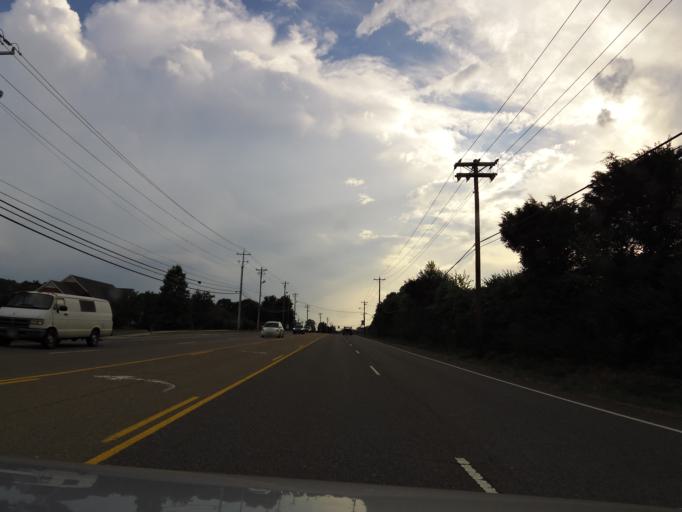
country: US
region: Tennessee
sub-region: Knox County
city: Farragut
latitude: 35.8760
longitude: -84.1724
